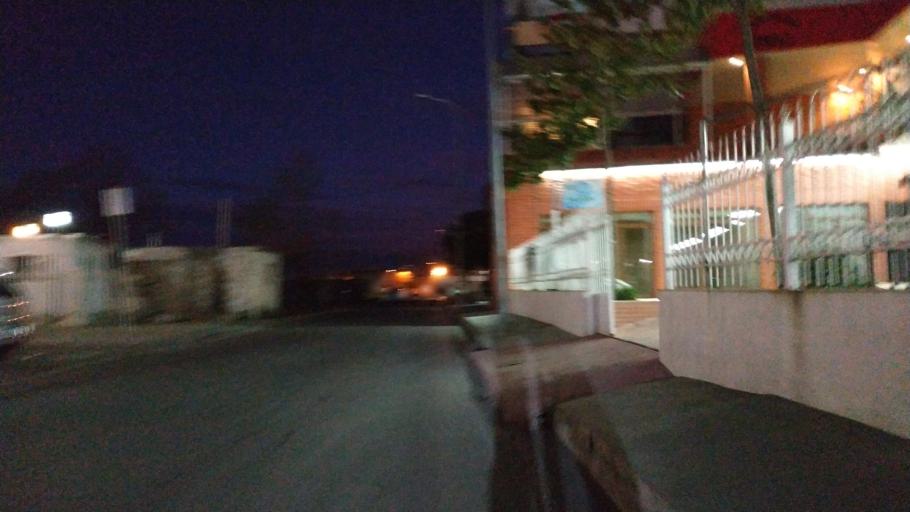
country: AL
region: Shkoder
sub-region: Rrethi i Shkodres
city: Shkoder
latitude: 42.0560
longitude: 19.4994
